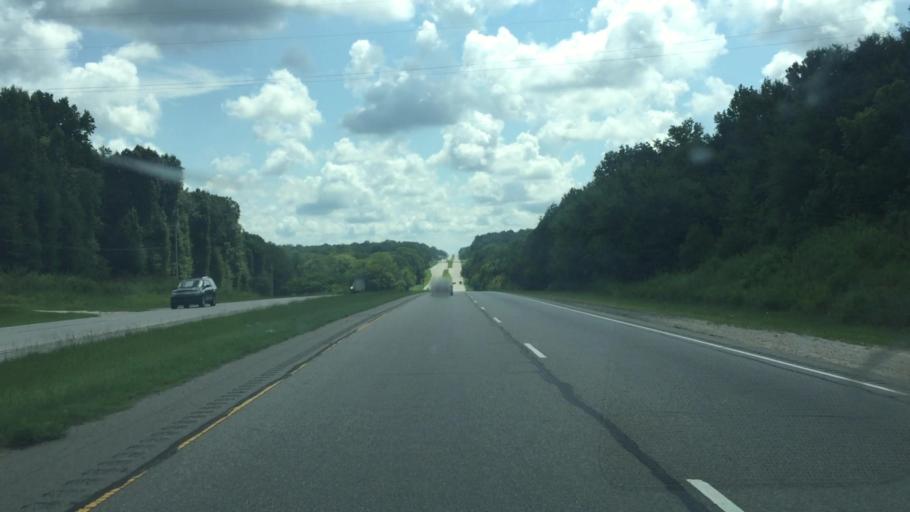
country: US
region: North Carolina
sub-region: Anson County
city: Wadesboro
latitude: 34.9638
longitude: -80.0266
